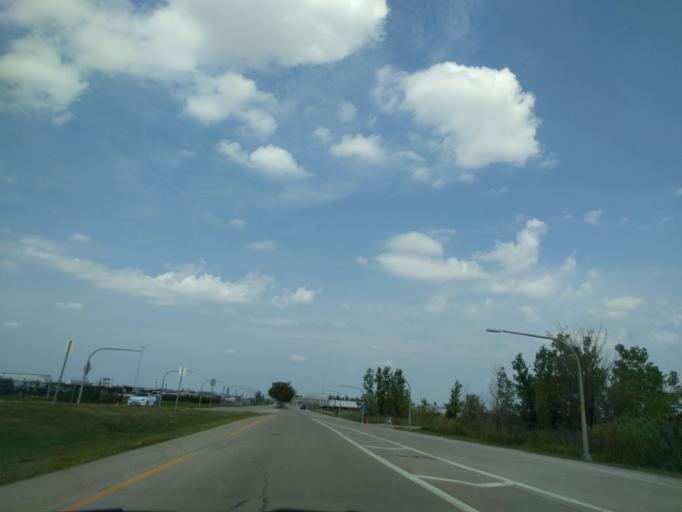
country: US
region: Illinois
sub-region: Cook County
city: Schiller Park
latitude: 41.9719
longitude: -87.8758
